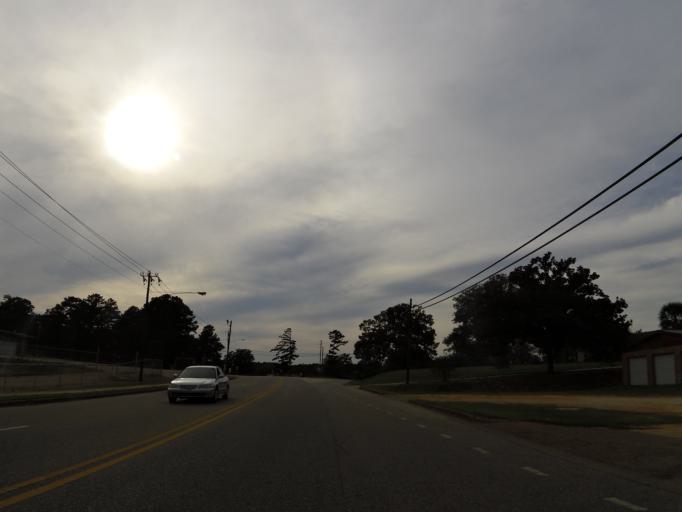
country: US
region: Alabama
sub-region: Monroe County
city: Monroeville
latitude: 31.5269
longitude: -87.3387
